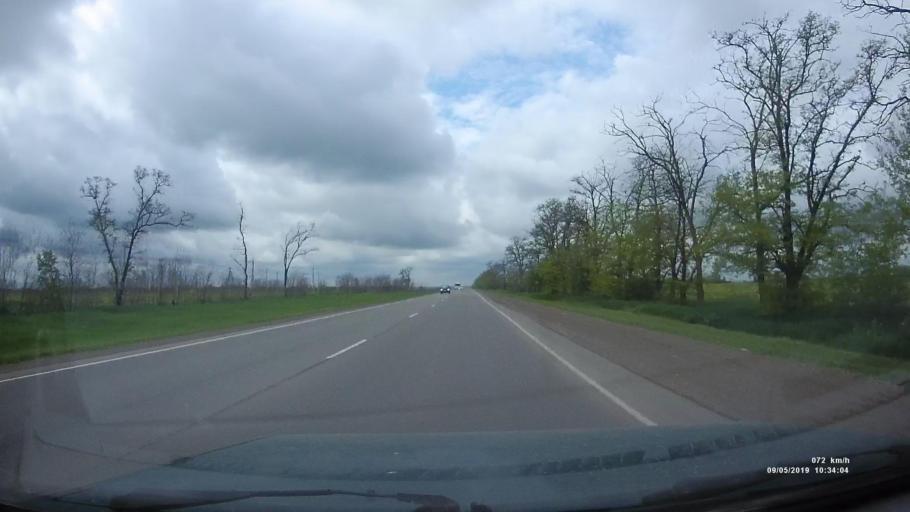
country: RU
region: Rostov
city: Azov
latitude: 47.0582
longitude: 39.4222
